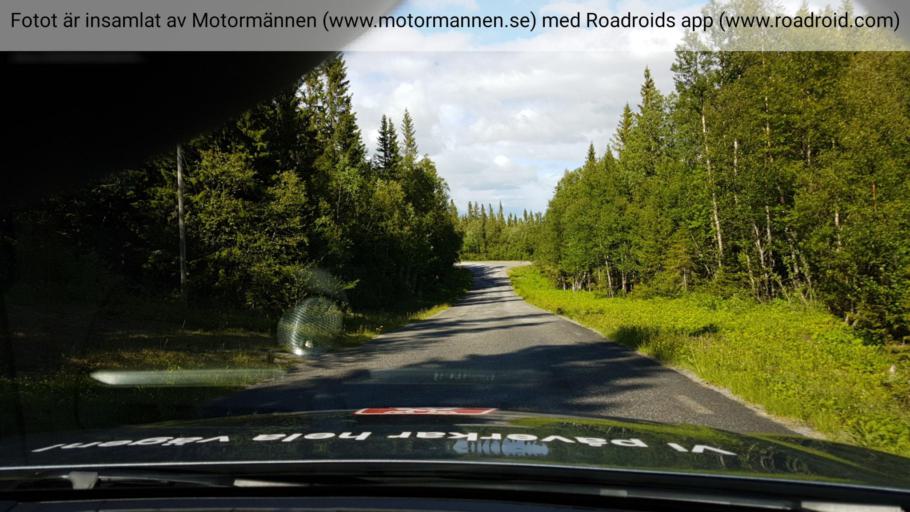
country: SE
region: Jaemtland
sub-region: Bergs Kommun
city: Hoverberg
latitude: 63.0161
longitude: 13.9442
